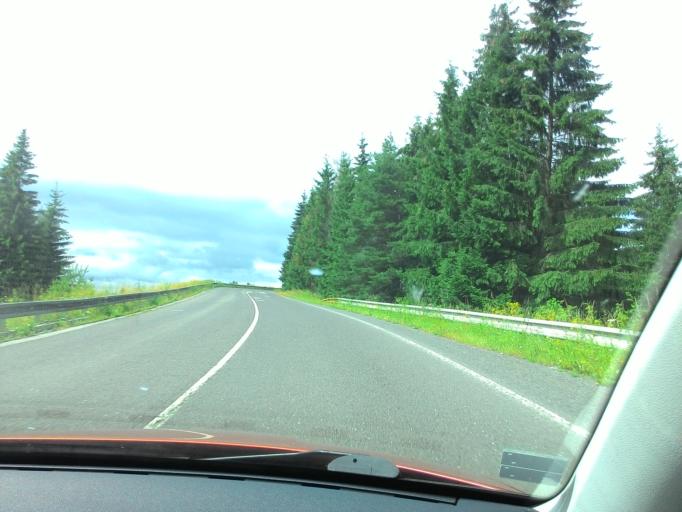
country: SK
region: Zilinsky
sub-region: Okres Liptovsky Mikulas
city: Hybe
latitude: 49.0660
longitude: 19.9192
